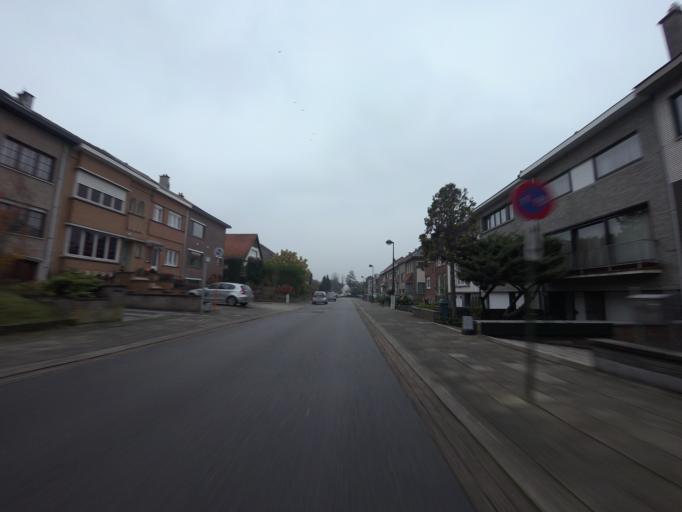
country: BE
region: Flanders
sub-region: Provincie Vlaams-Brabant
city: Zaventem
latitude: 50.8792
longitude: 4.4711
